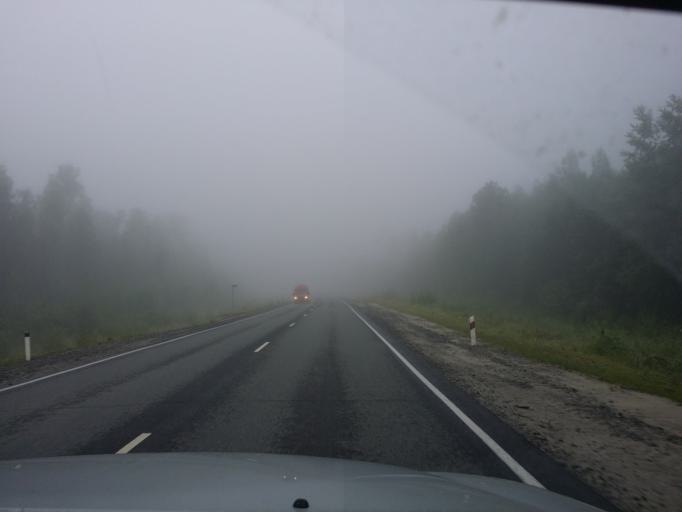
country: RU
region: Khanty-Mansiyskiy Avtonomnyy Okrug
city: Gornopravdinsk
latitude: 59.6628
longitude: 69.9747
